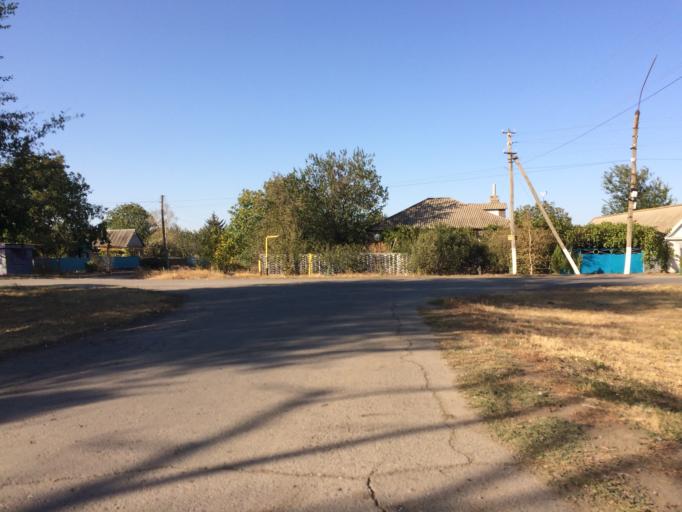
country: RU
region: Rostov
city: Tselina
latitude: 46.5189
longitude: 41.1840
